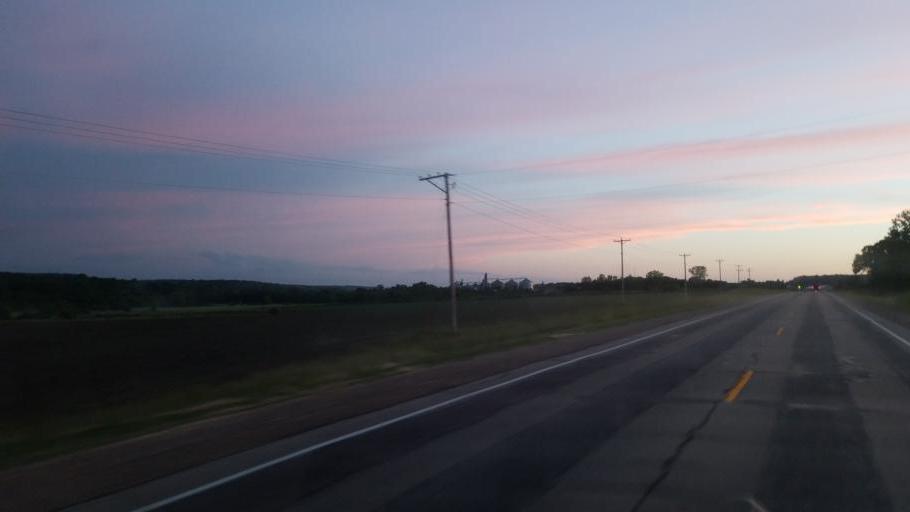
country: US
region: Wisconsin
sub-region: Vernon County
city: Hillsboro
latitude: 43.6780
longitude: -90.3031
